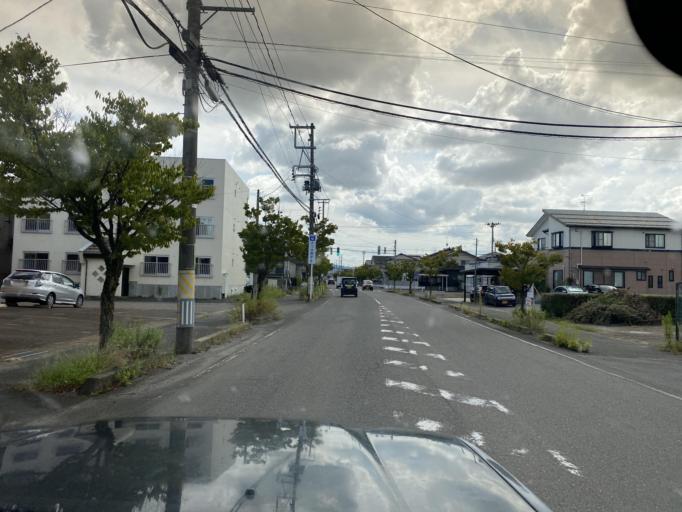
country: JP
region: Niigata
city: Niitsu-honcho
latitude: 37.8136
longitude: 139.1161
